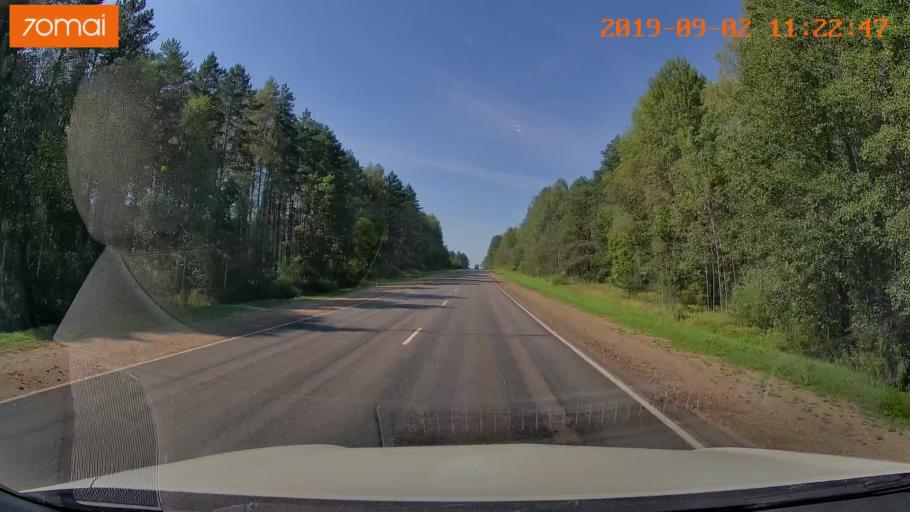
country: RU
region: Smolensk
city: Roslavl'
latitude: 54.0227
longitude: 33.0056
